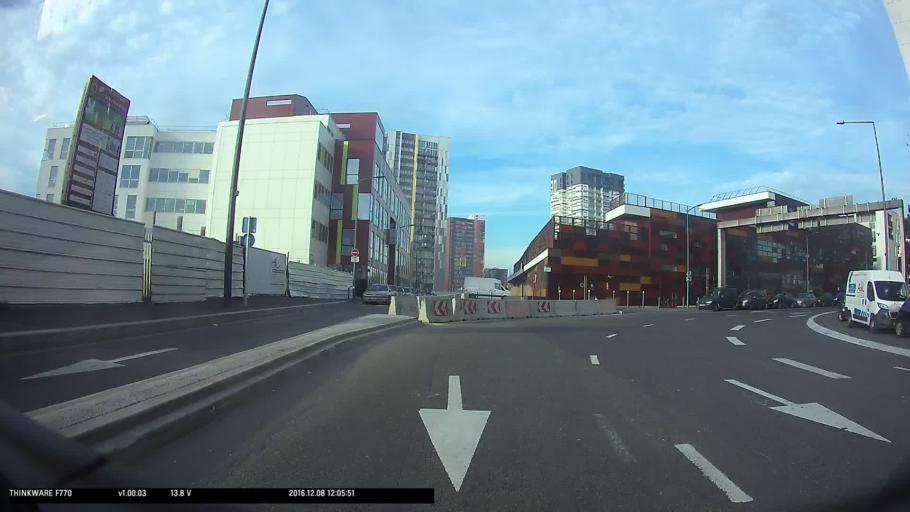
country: FR
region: Ile-de-France
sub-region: Departement de Seine-Saint-Denis
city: Bobigny
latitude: 48.9040
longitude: 2.4447
